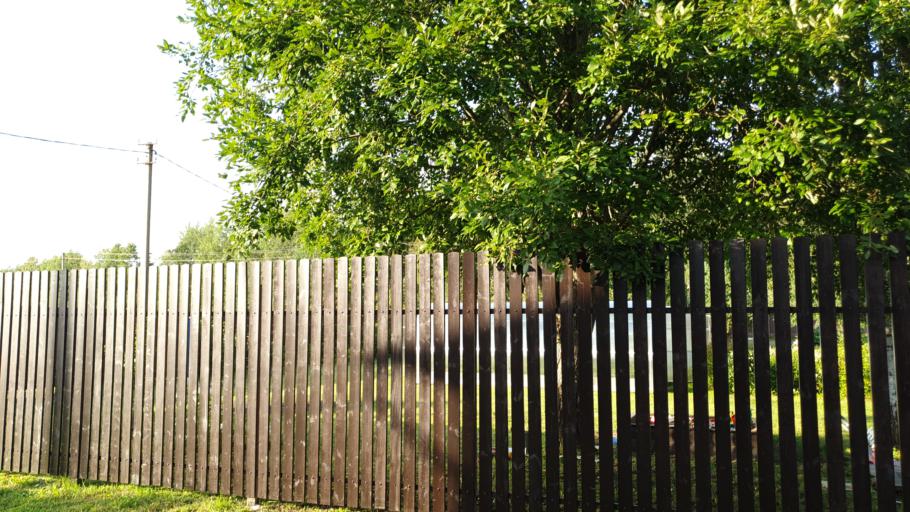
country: RU
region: Leningrad
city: Ivangorod
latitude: 59.4244
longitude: 28.3314
